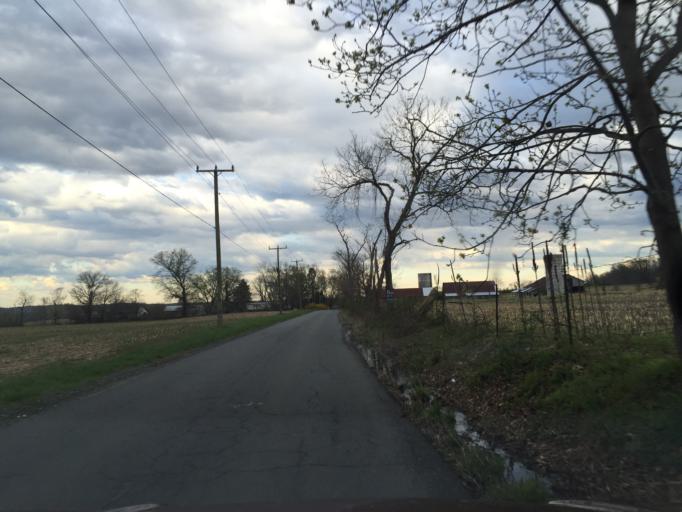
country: US
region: Maryland
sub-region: Frederick County
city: Point of Rocks
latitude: 39.2104
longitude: -77.5441
